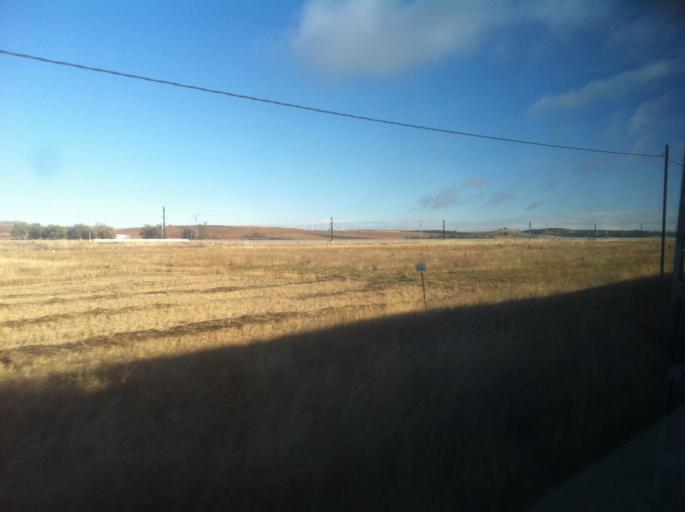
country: ES
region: Castille and Leon
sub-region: Provincia de Palencia
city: Villodrigo
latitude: 42.1445
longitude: -4.1107
